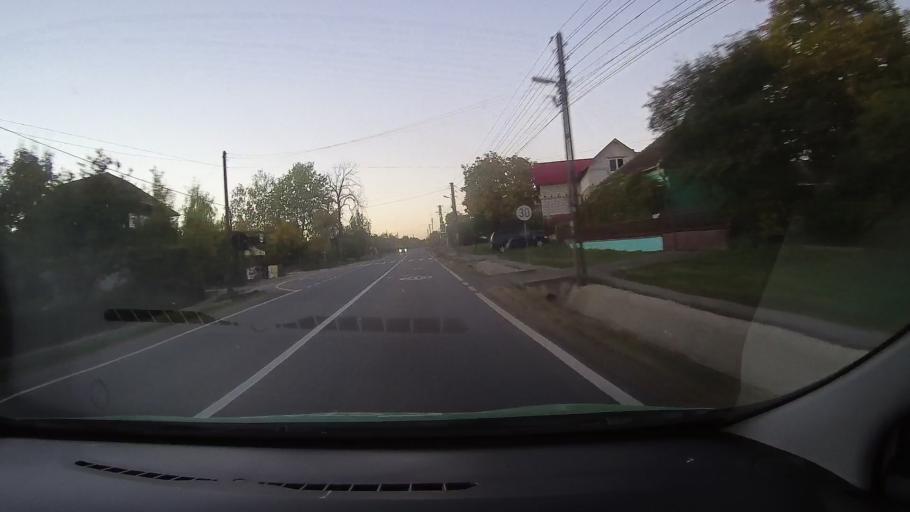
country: RO
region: Bihor
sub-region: Comuna Tarcea
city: Tarcea
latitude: 47.4621
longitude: 22.1684
